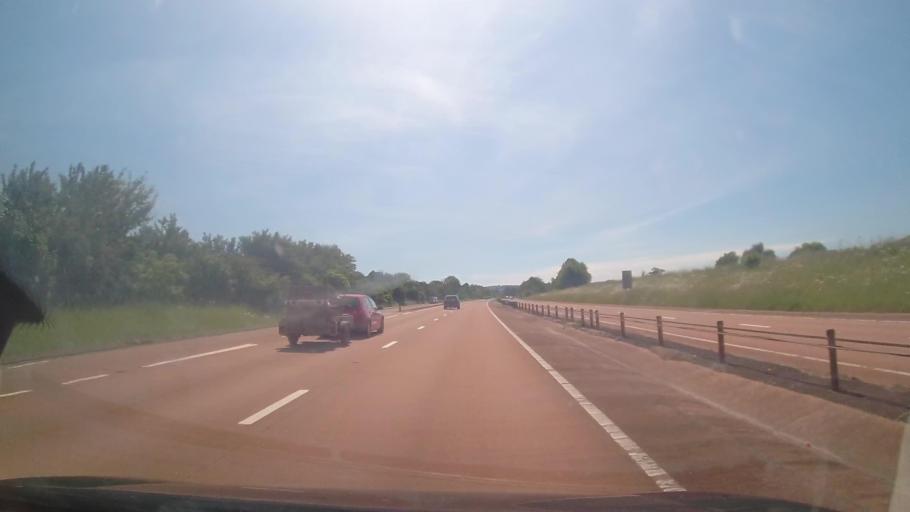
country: GB
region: England
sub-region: Devon
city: Ottery St Mary
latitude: 50.7738
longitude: -3.2790
